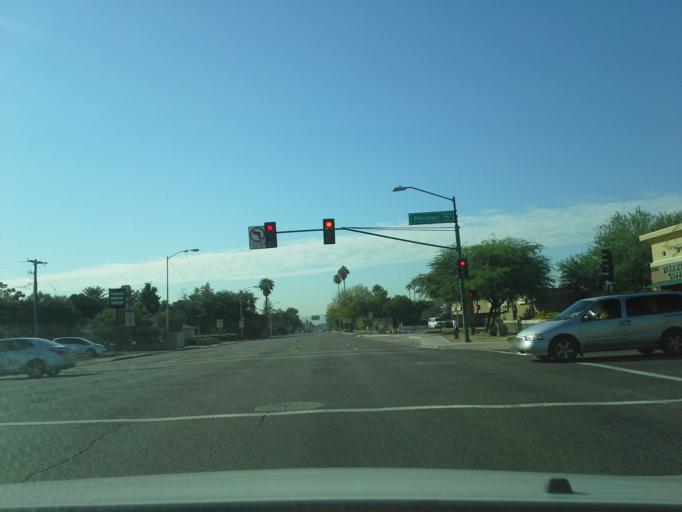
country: US
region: Arizona
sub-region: Maricopa County
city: Phoenix
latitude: 33.5169
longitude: -112.0825
